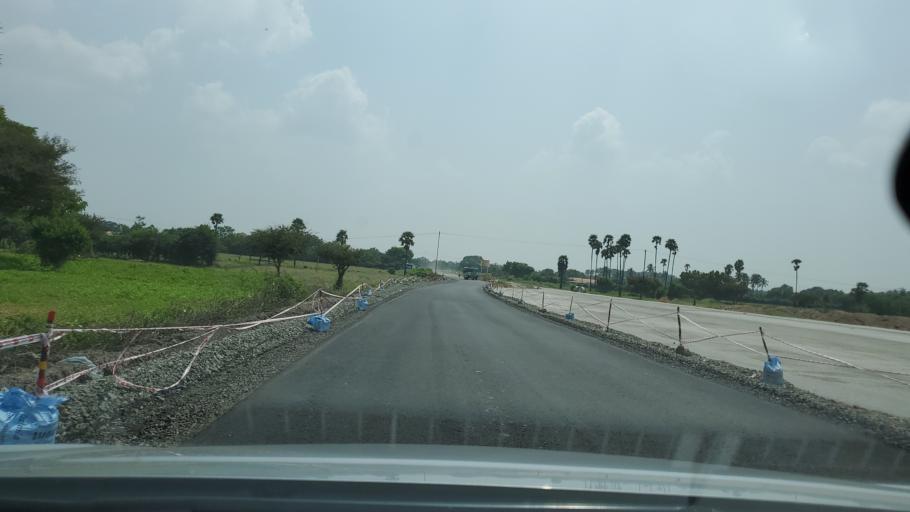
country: IN
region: Tamil Nadu
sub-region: Tiruppur
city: Dharapuram
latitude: 10.8095
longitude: 77.4845
